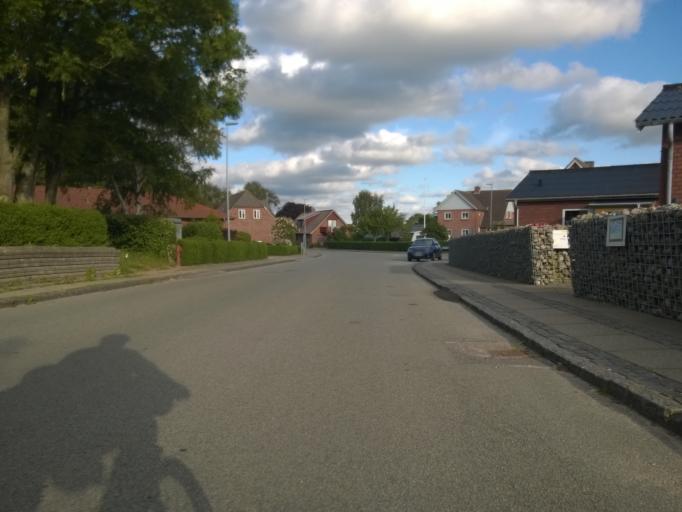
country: DK
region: Central Jutland
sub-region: Holstebro Kommune
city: Vinderup
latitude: 56.4355
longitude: 8.7762
